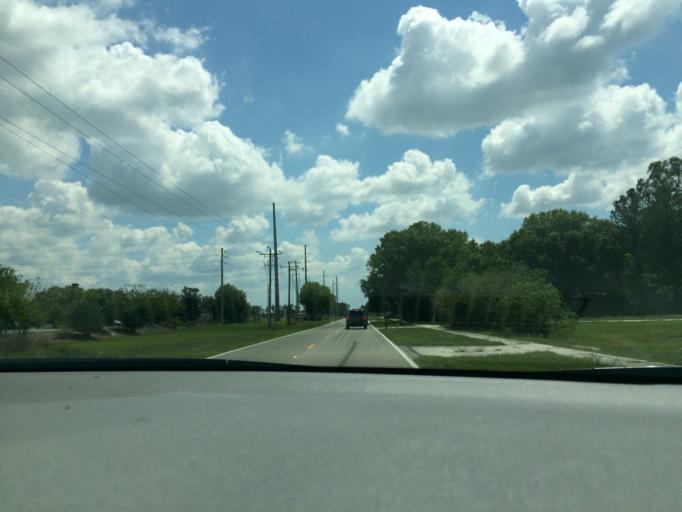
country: US
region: Florida
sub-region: Sarasota County
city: The Meadows
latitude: 27.4369
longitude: -82.3954
